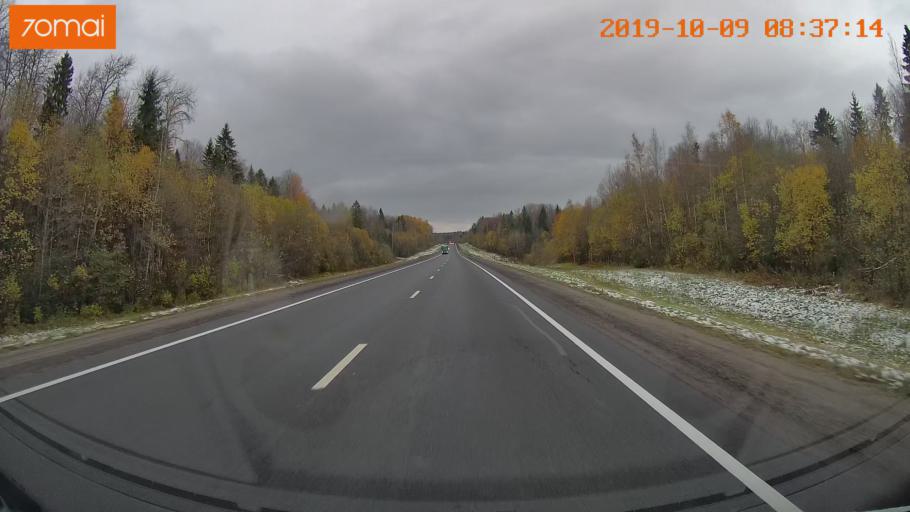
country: RU
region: Vologda
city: Gryazovets
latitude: 58.9382
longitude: 40.1752
